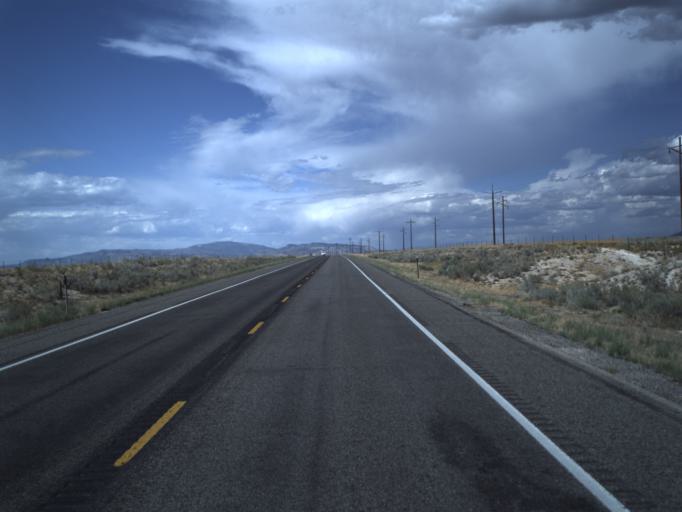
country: US
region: Utah
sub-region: Sevier County
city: Salina
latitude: 39.0180
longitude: -111.8339
